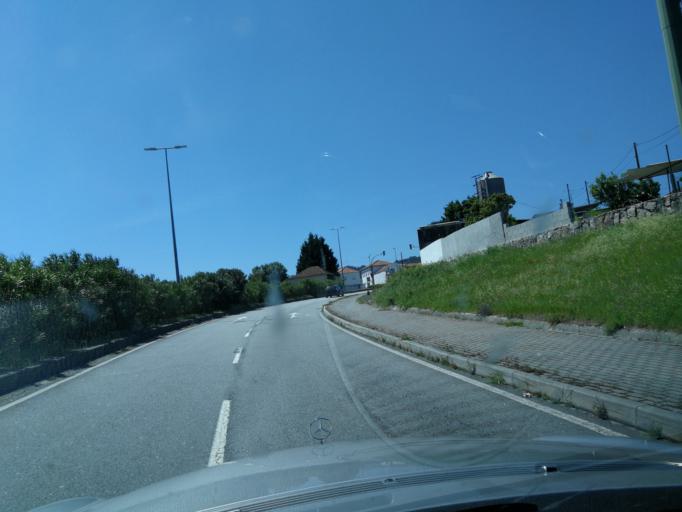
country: PT
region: Viana do Castelo
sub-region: Viana do Castelo
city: Meadela
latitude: 41.7096
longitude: -8.8057
